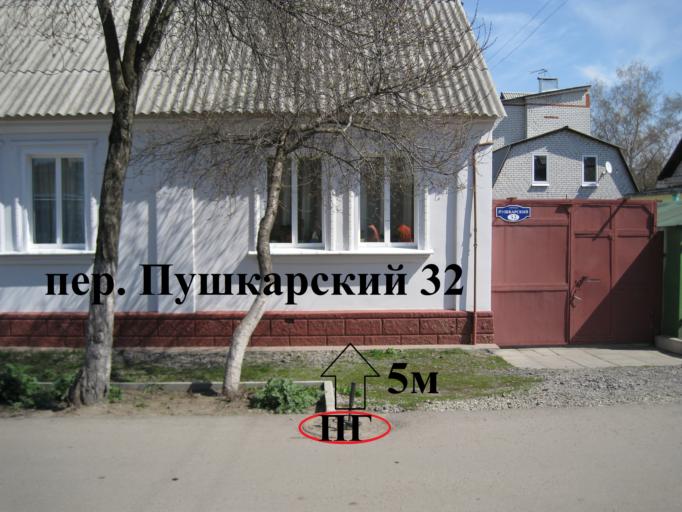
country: RU
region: Voronezj
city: Voronezh
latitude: 51.6472
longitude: 39.1773
